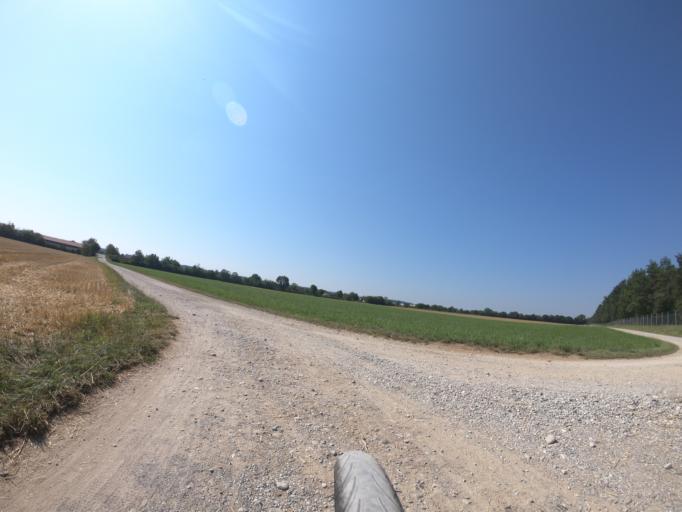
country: DE
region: Bavaria
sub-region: Upper Bavaria
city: Emmering
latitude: 48.1940
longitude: 11.2773
